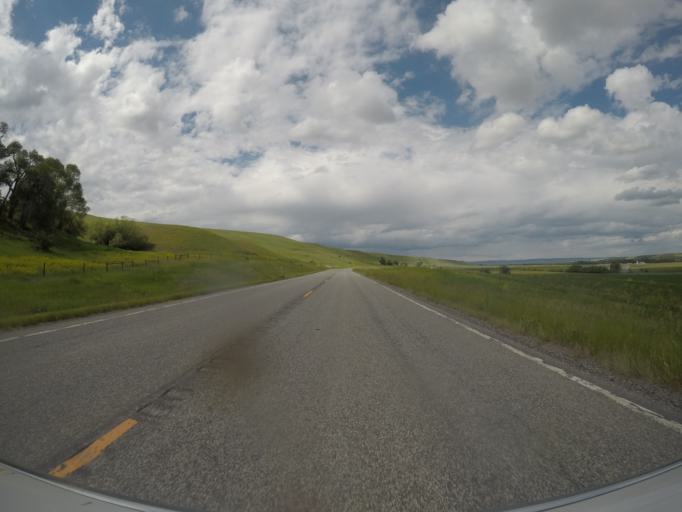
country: US
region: Montana
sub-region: Sweet Grass County
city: Big Timber
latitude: 45.7686
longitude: -109.9899
